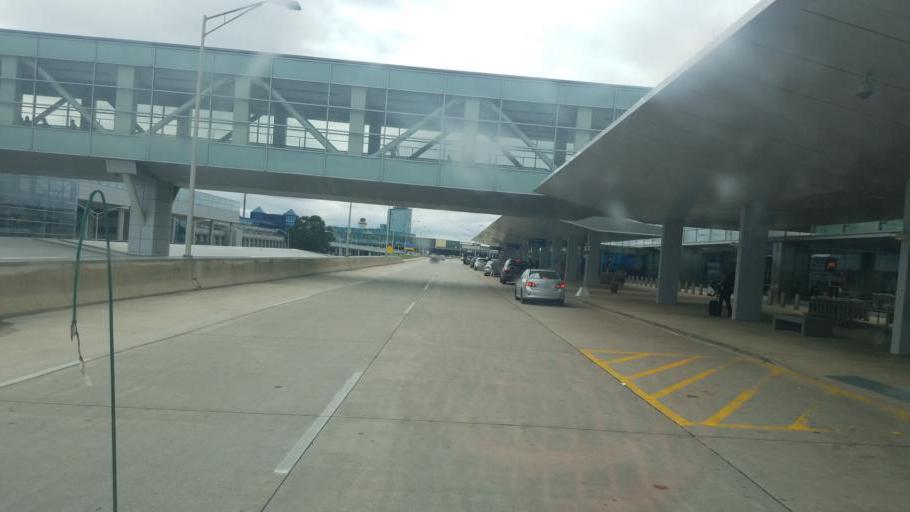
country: US
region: Michigan
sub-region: Wayne County
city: Romulus
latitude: 42.2259
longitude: -83.3474
